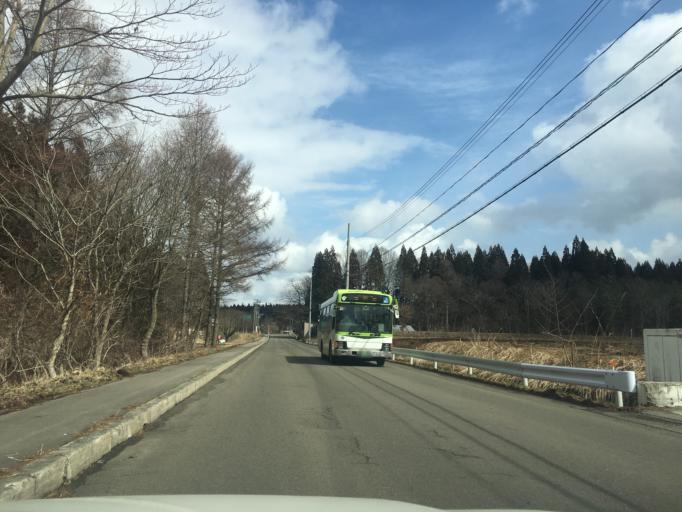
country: JP
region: Akita
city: Takanosu
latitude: 40.1864
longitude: 140.3401
